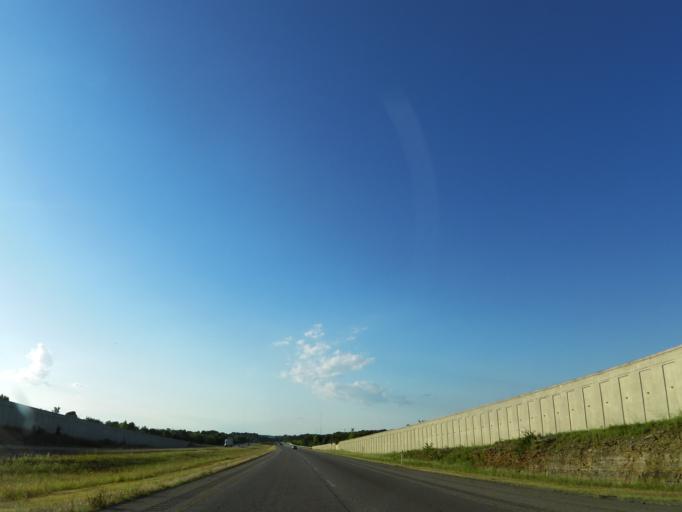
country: US
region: Tennessee
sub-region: Wilson County
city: Rural Hill
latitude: 36.0407
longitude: -86.4291
